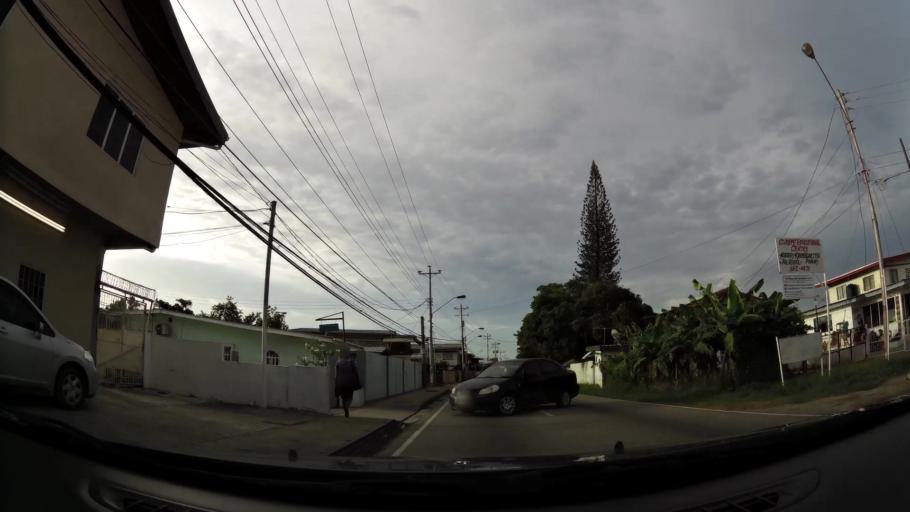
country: TT
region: Tunapuna/Piarco
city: Tunapuna
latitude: 10.6421
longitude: -61.4102
